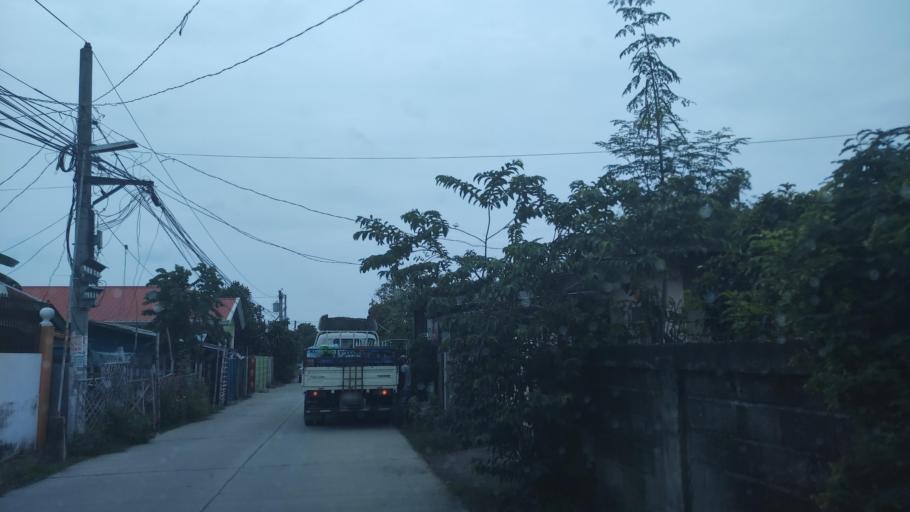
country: PH
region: Central Luzon
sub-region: Province of Nueva Ecija
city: San Anton
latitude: 15.3589
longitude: 120.9032
